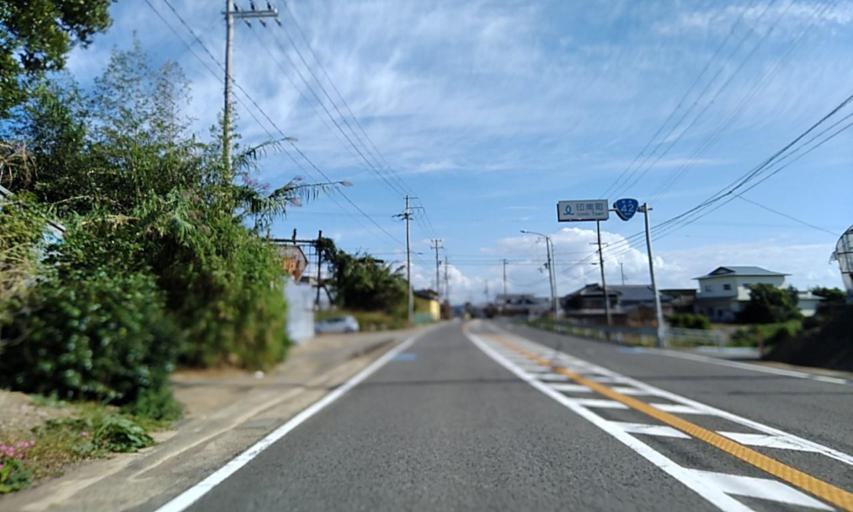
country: JP
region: Wakayama
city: Gobo
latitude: 33.8159
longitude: 135.1995
